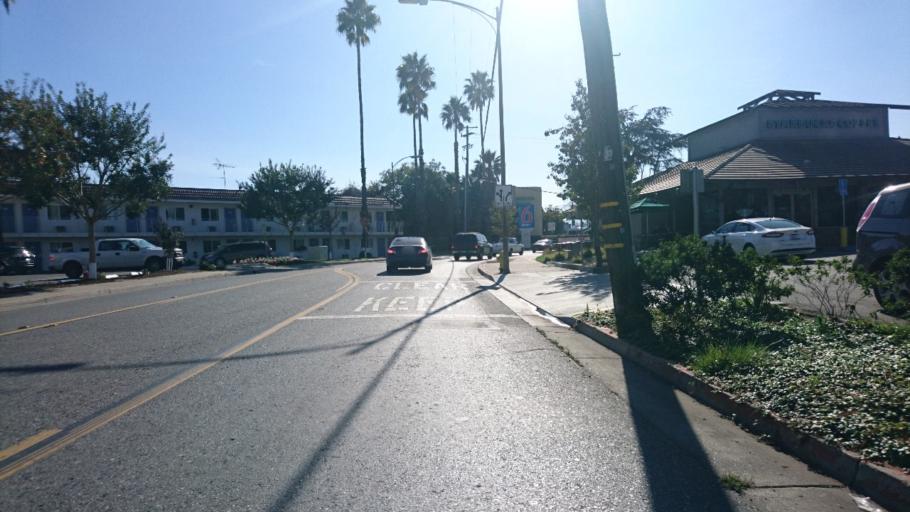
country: US
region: California
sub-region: Santa Clara County
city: Campbell
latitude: 37.2710
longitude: -121.9463
